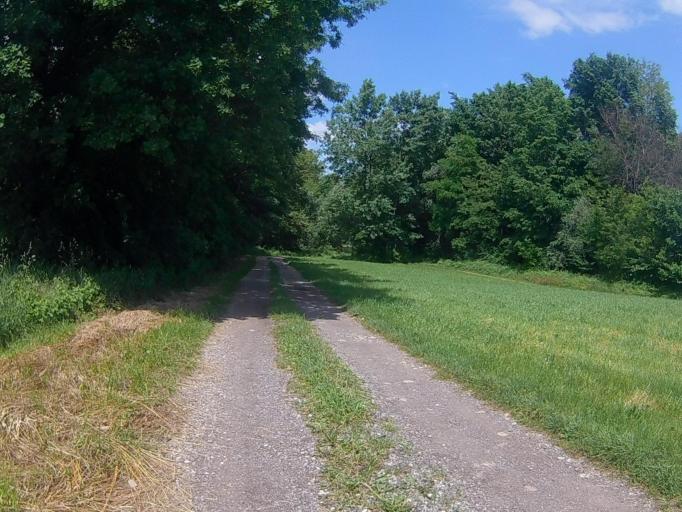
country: SI
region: Miklavz na Dravskem Polju
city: Miklavz na Dravskem Polju
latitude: 46.5129
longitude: 15.7037
